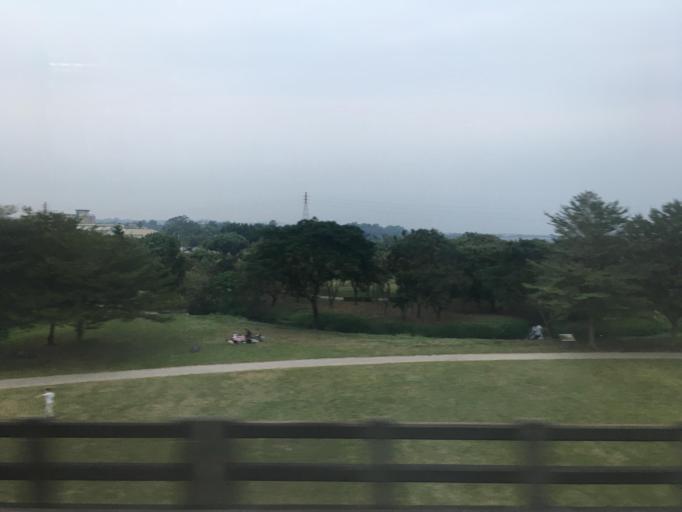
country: TW
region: Taiwan
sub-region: Pingtung
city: Pingtung
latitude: 22.6625
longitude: 120.4283
